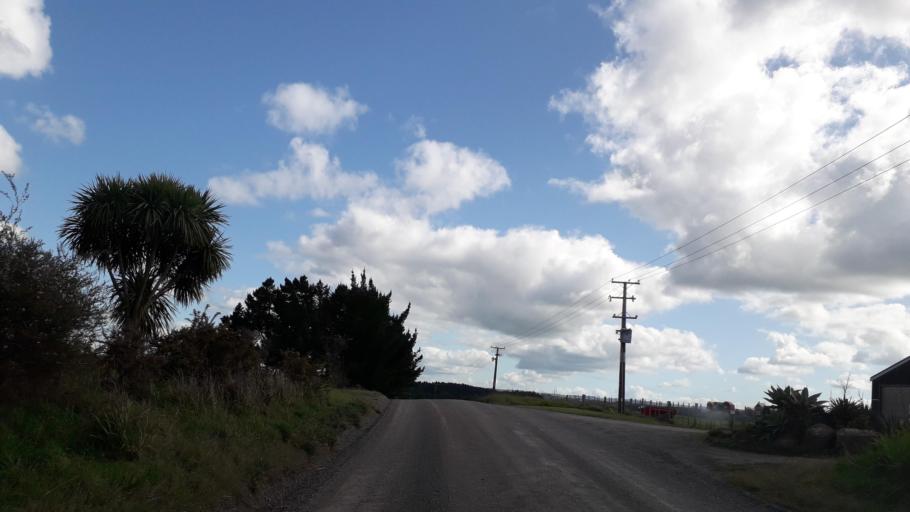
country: NZ
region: Northland
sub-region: Far North District
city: Kerikeri
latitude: -35.1333
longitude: 174.0002
